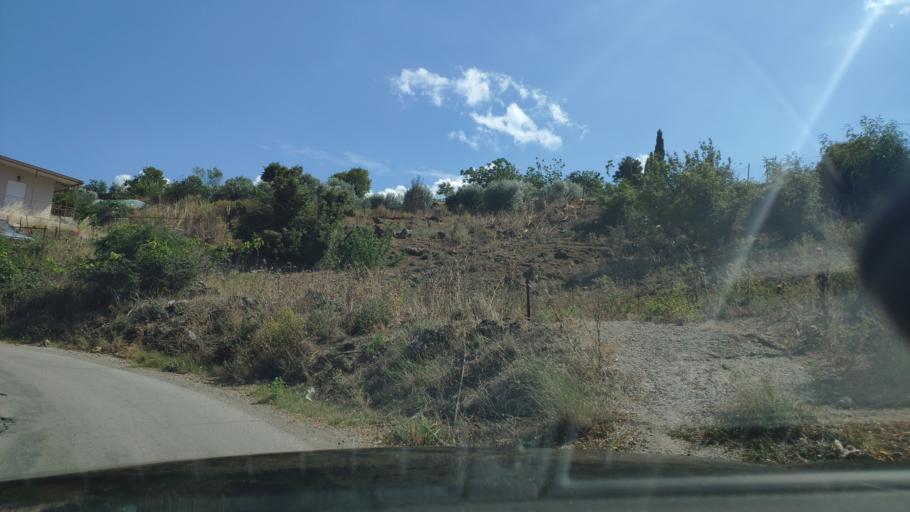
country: GR
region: West Greece
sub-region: Nomos Aitolias kai Akarnanias
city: Katouna
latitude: 38.7912
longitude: 21.1148
